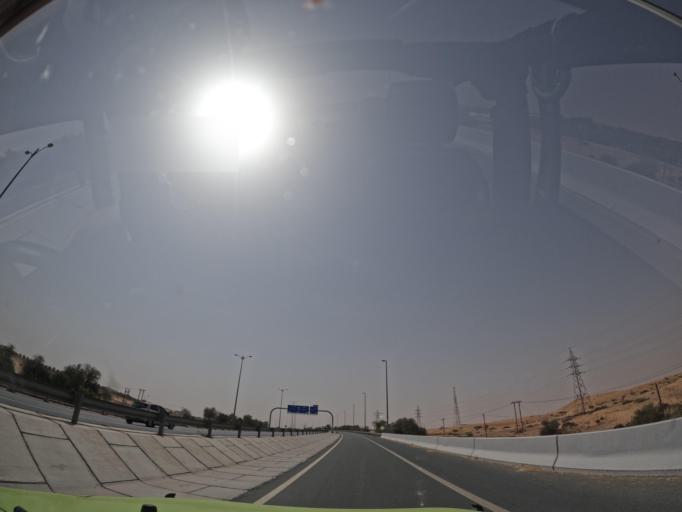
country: OM
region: Al Buraimi
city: Al Buraymi
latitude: 24.6950
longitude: 55.6290
